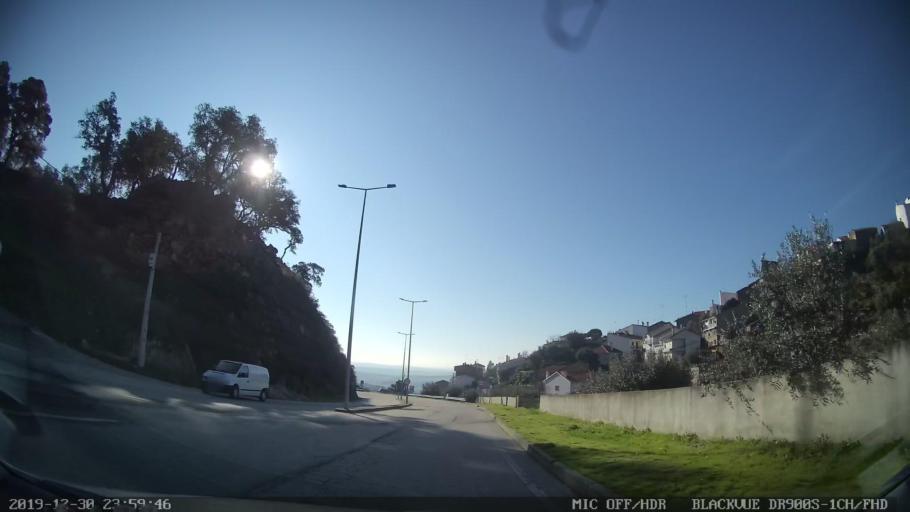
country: PT
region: Castelo Branco
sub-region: Idanha-A-Nova
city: Idanha-a-Nova
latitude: 39.9240
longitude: -7.2339
